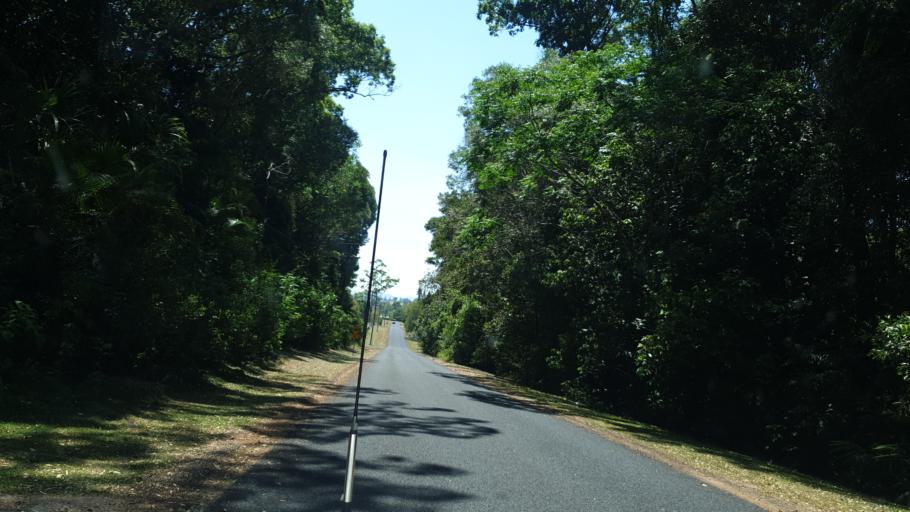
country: AU
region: Queensland
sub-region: Tablelands
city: Atherton
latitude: -17.3417
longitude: 145.6259
